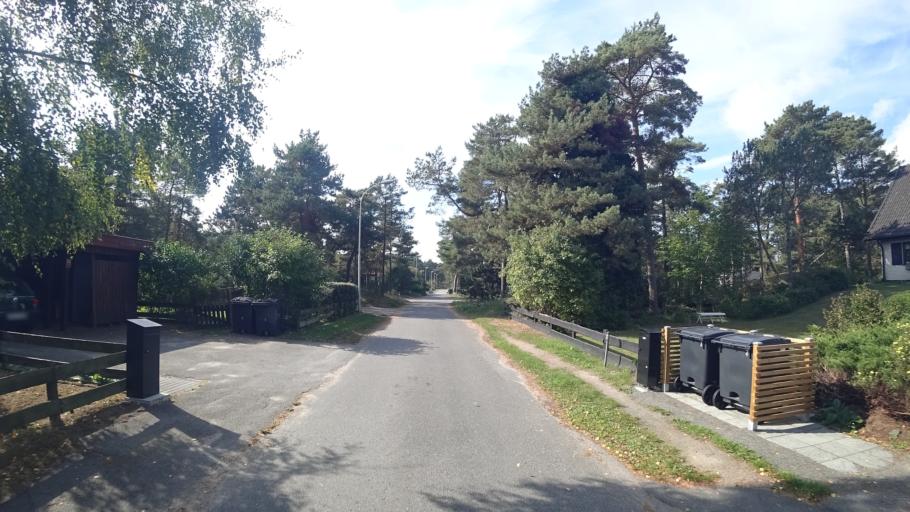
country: SE
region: Skane
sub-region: Kristianstads Kommun
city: Ahus
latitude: 55.9125
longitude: 14.2874
